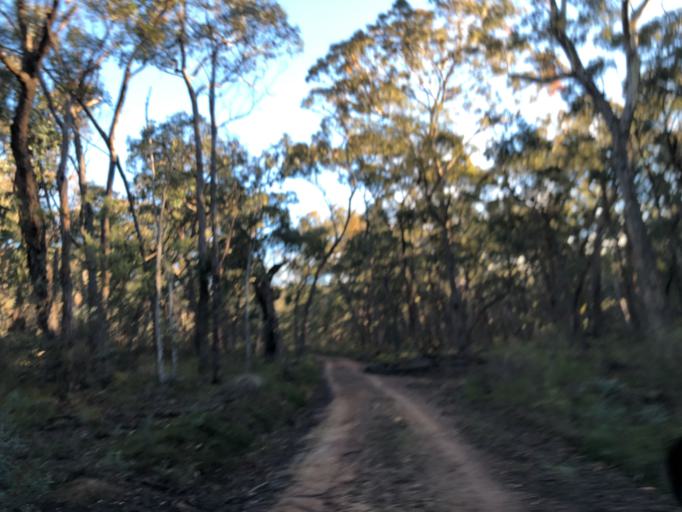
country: AU
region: Victoria
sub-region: Mount Alexander
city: Castlemaine
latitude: -37.2317
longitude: 144.2735
